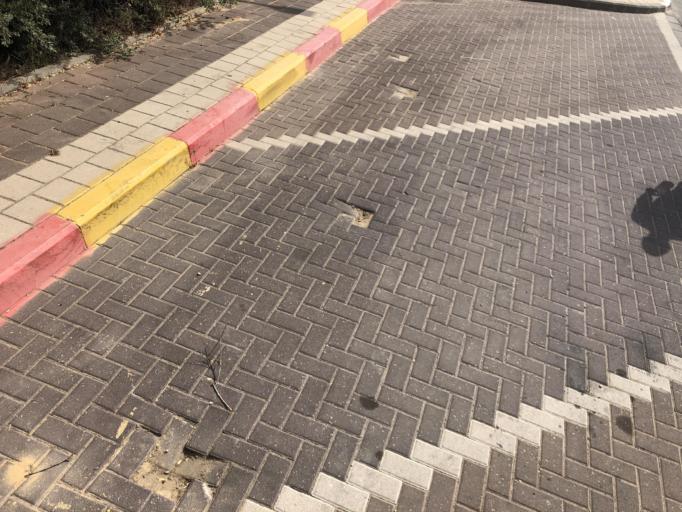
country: PS
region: West Bank
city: Jit
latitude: 32.2157
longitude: 35.1586
